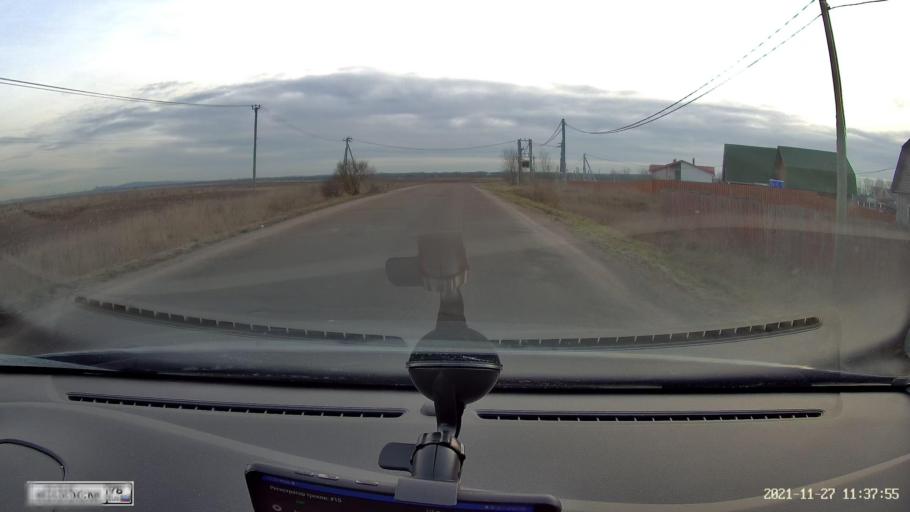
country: RU
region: Leningrad
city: Russko-Vysotskoye
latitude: 59.6920
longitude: 29.9932
